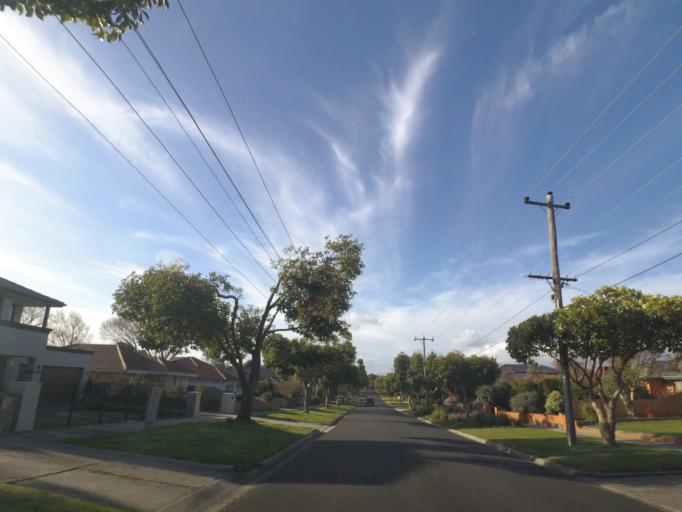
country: AU
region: Victoria
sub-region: Whitehorse
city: Box Hill North
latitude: -37.8020
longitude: 145.1338
